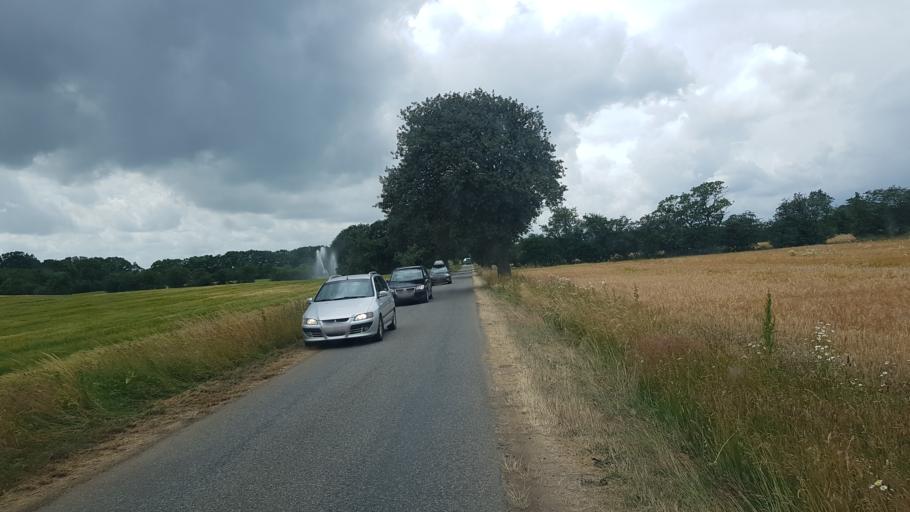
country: DK
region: South Denmark
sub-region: Kolding Kommune
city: Lunderskov
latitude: 55.5028
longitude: 9.3129
